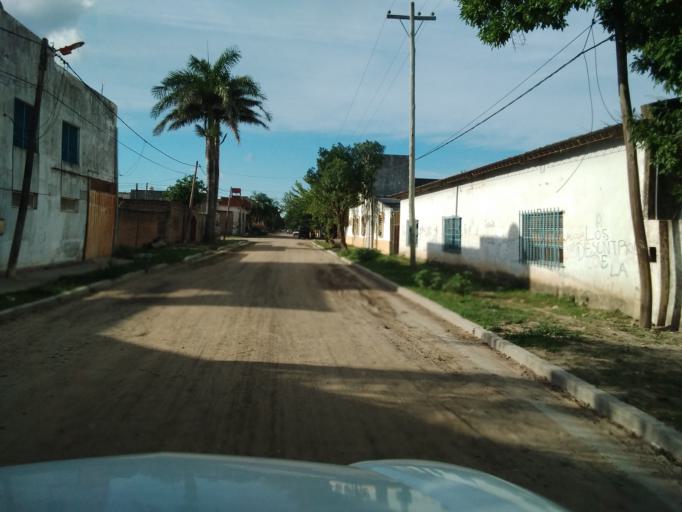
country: AR
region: Corrientes
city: Corrientes
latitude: -27.4902
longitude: -58.8444
